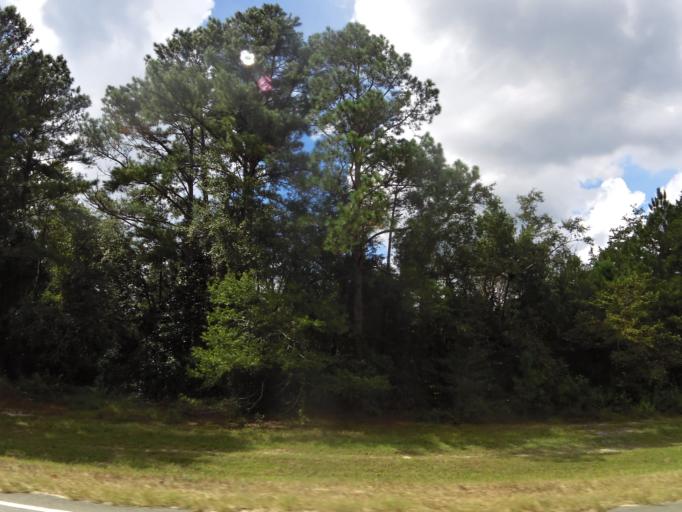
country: US
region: Georgia
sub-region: Brantley County
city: Nahunta
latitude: 31.1608
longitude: -81.9912
